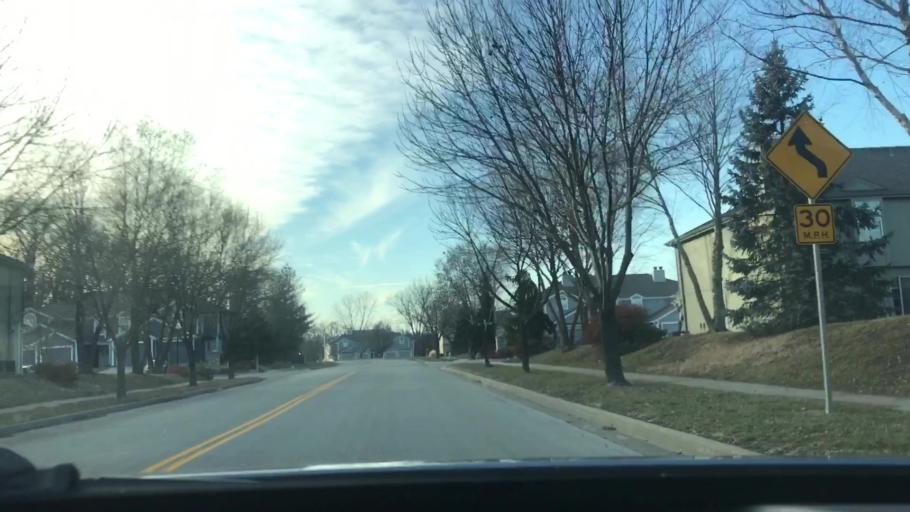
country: US
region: Missouri
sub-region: Jackson County
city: East Independence
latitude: 39.0171
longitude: -94.3782
